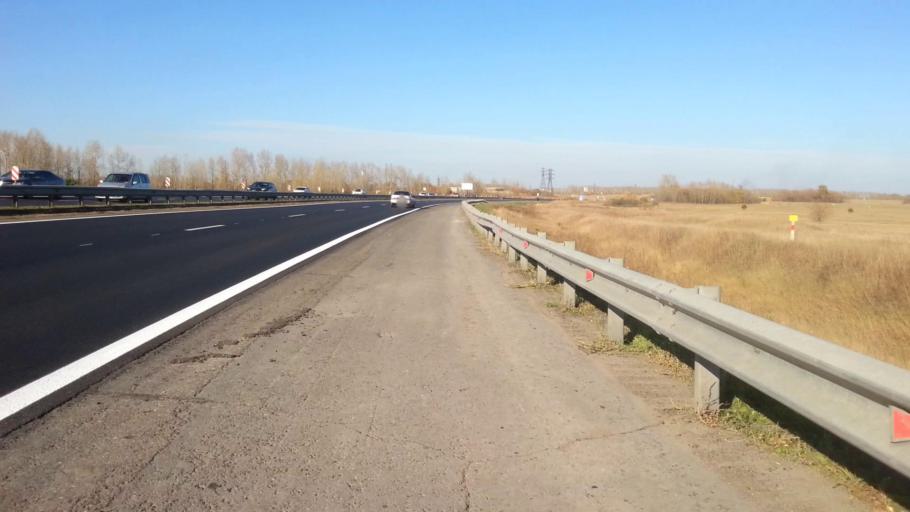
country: RU
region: Altai Krai
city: Novoaltaysk
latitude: 53.3646
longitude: 83.9476
